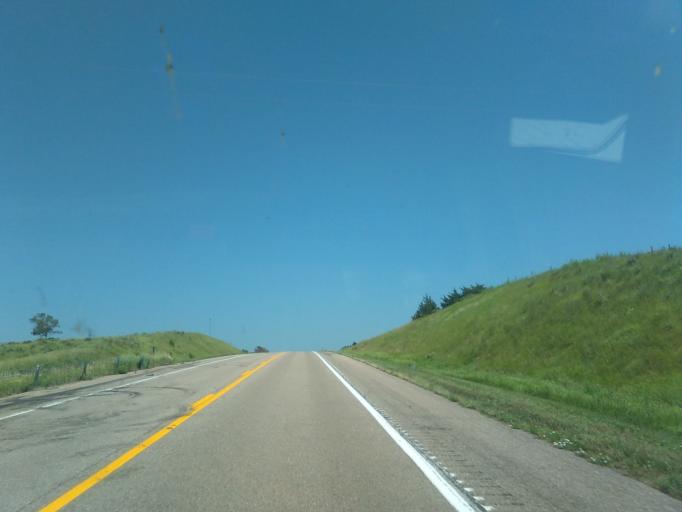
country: US
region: Nebraska
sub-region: Frontier County
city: Stockville
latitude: 40.5871
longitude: -100.6295
